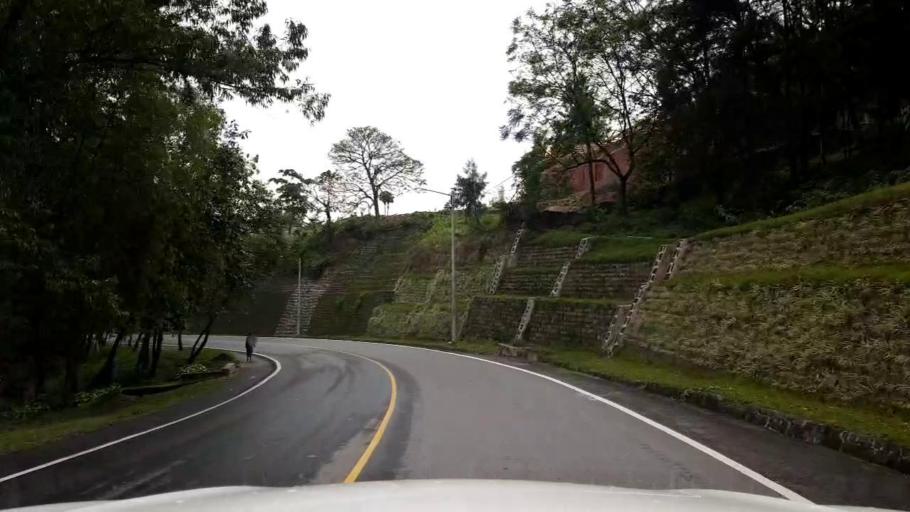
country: RW
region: Western Province
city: Gisenyi
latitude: -1.7026
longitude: 29.2712
